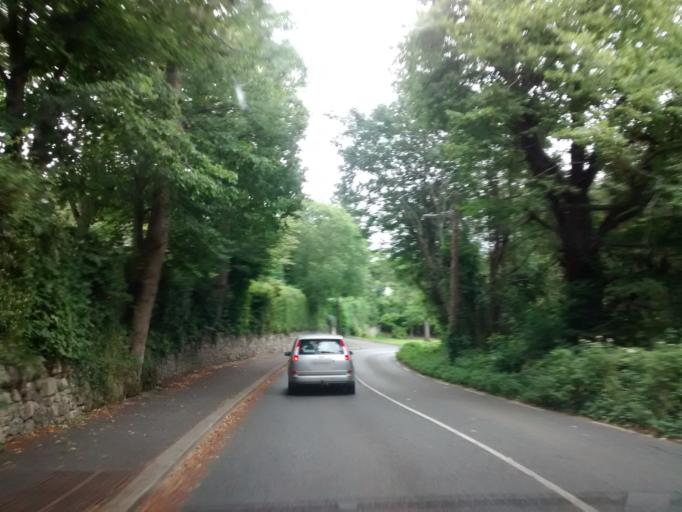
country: IE
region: Leinster
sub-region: Wicklow
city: Enniskerry
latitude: 53.1949
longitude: -6.1712
